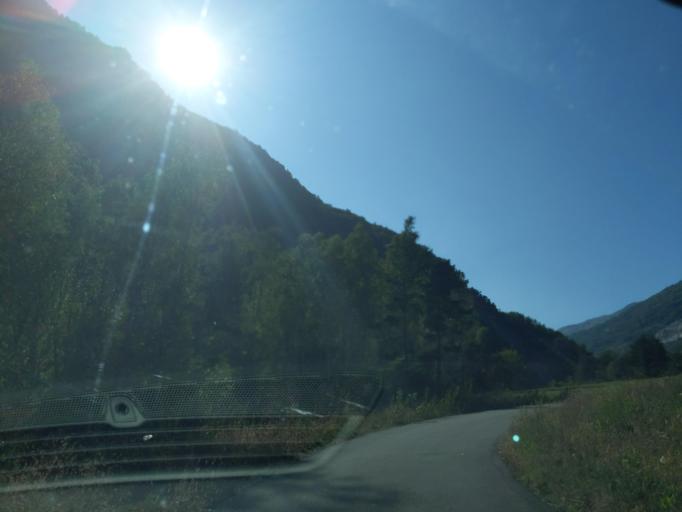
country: FR
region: Rhone-Alpes
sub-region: Departement de la Savoie
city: Saint-Jean-de-Maurienne
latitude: 45.2675
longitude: 6.3488
